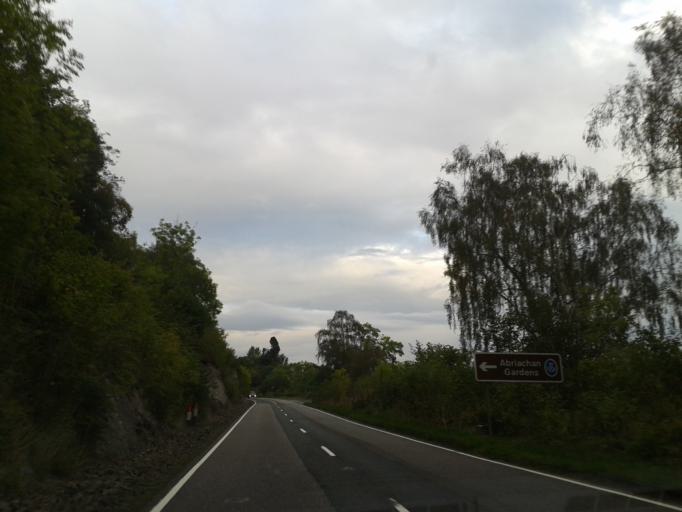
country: GB
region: Scotland
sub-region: Highland
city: Beauly
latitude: 57.3772
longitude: -4.3811
